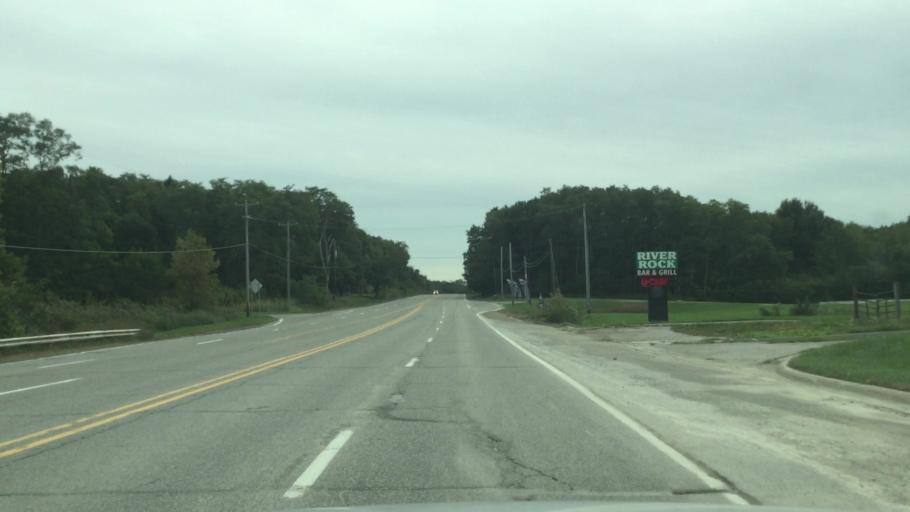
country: US
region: Michigan
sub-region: Oakland County
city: Holly
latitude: 42.8156
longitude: -83.5469
